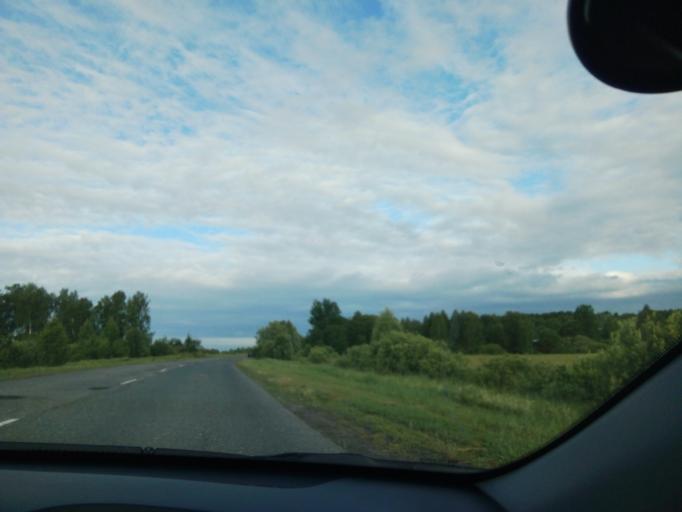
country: RU
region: Rjazan
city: Yermish'
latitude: 54.7851
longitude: 42.4399
